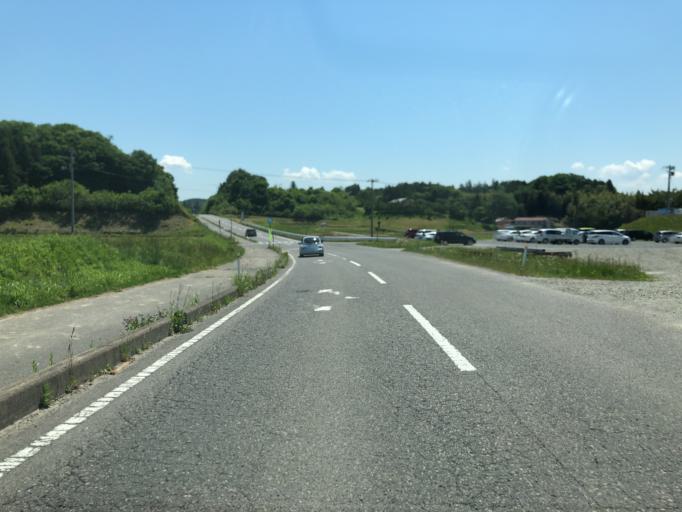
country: JP
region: Fukushima
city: Motomiya
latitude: 37.5284
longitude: 140.4328
